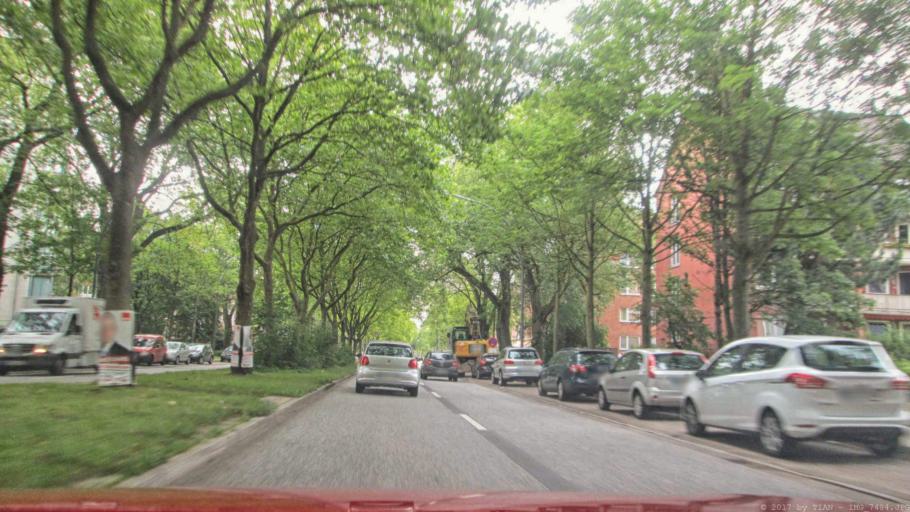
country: DE
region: Hamburg
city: Marienthal
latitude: 53.5567
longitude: 10.0787
